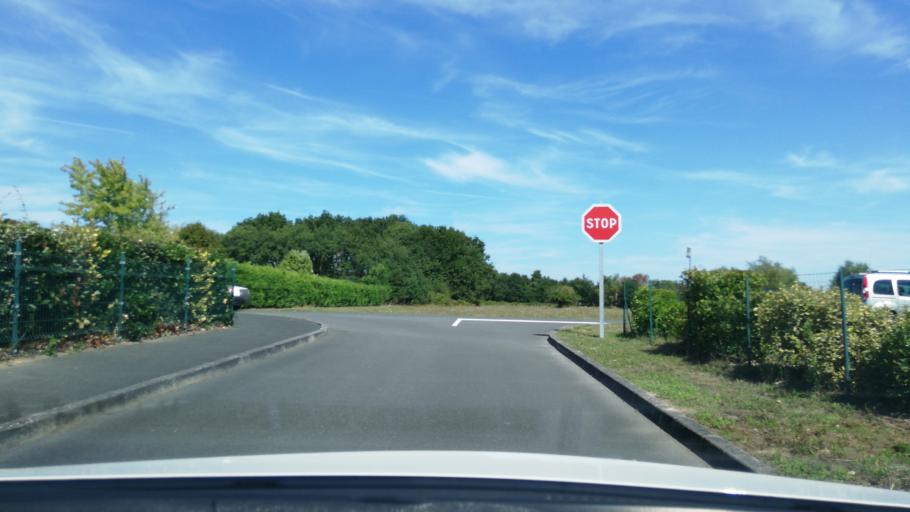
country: FR
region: Centre
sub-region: Departement d'Indre-et-Loire
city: Mazieres-de-Touraine
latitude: 47.3862
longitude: 0.4241
